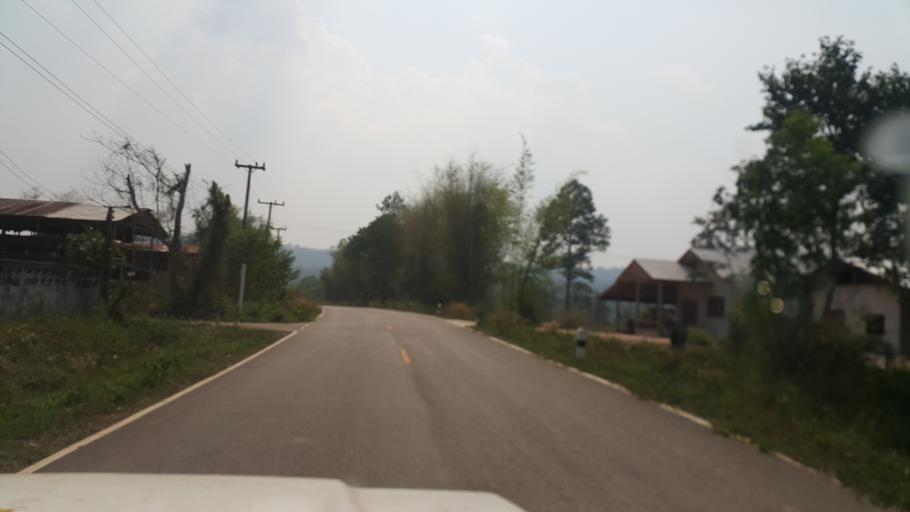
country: TH
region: Nakhon Phanom
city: Ban Phaeng
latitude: 17.9543
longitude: 104.1733
